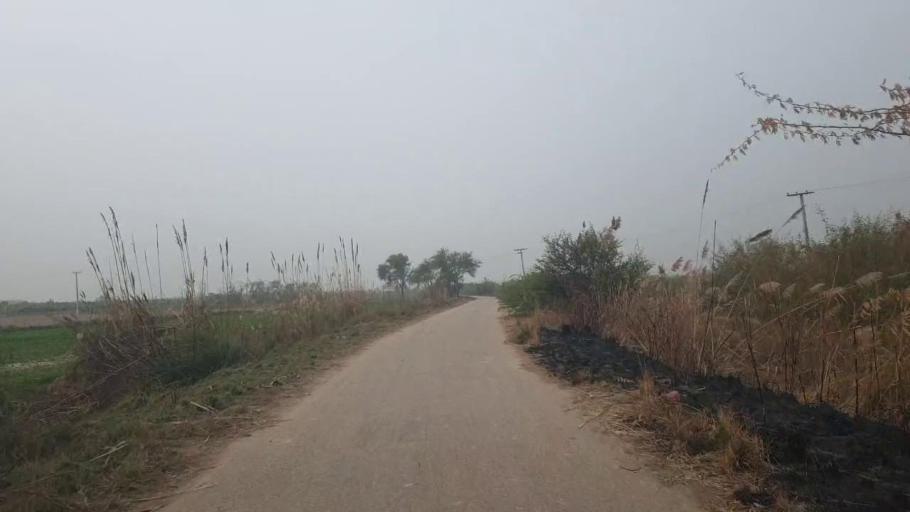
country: PK
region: Sindh
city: Tando Adam
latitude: 25.8159
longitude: 68.7151
